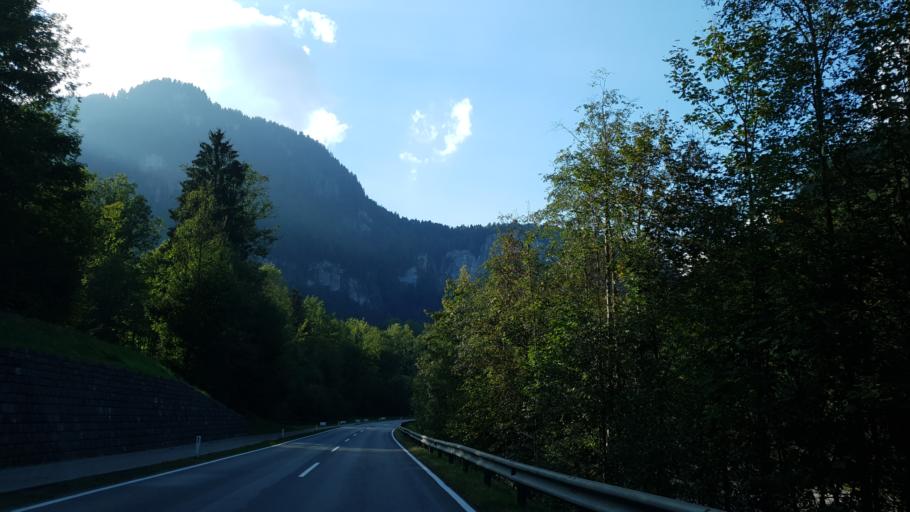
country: AT
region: Vorarlberg
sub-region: Politischer Bezirk Bregenz
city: Reuthe
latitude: 47.3857
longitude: 9.8619
